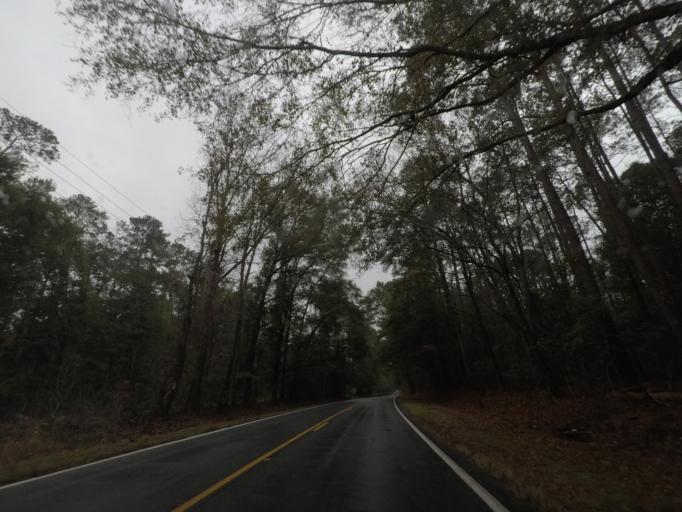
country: US
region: South Carolina
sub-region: Charleston County
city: Meggett
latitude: 32.7017
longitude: -80.3477
